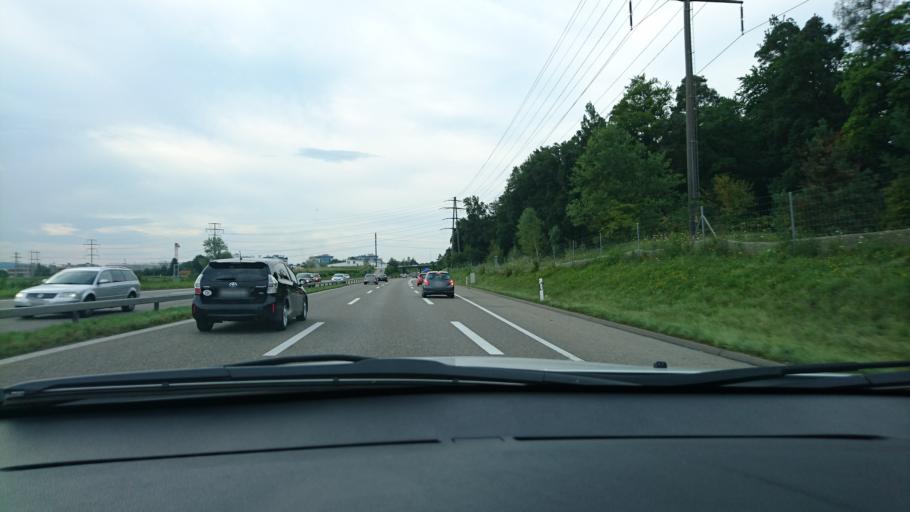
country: CH
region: Zurich
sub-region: Bezirk Uster
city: Naenikon / Naenikon (Dorfkern)
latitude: 47.3781
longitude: 8.6896
